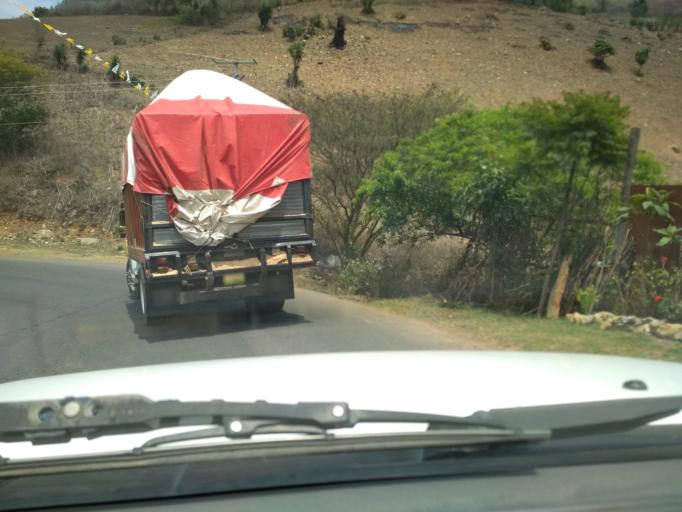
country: MX
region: Veracruz
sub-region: Acultzingo
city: Acatla
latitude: 18.7535
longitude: -97.1960
